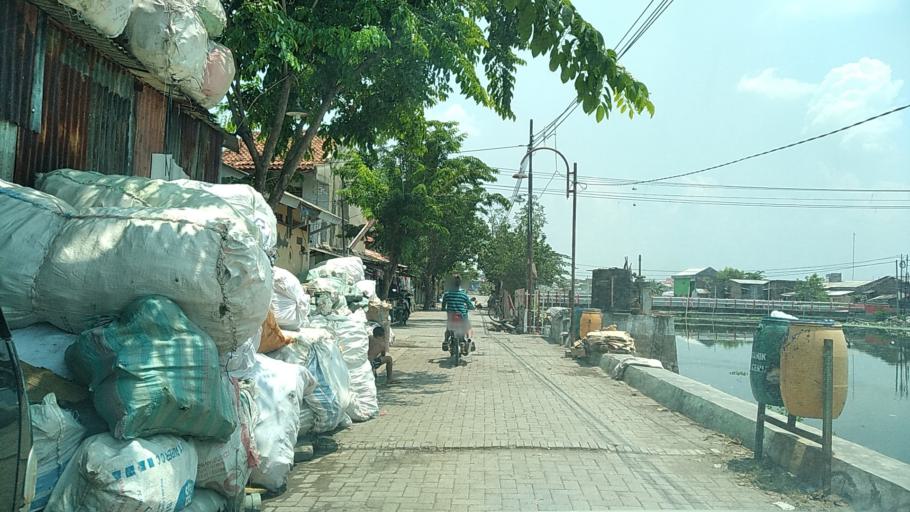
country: ID
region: Central Java
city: Semarang
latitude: -6.9532
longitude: 110.4378
